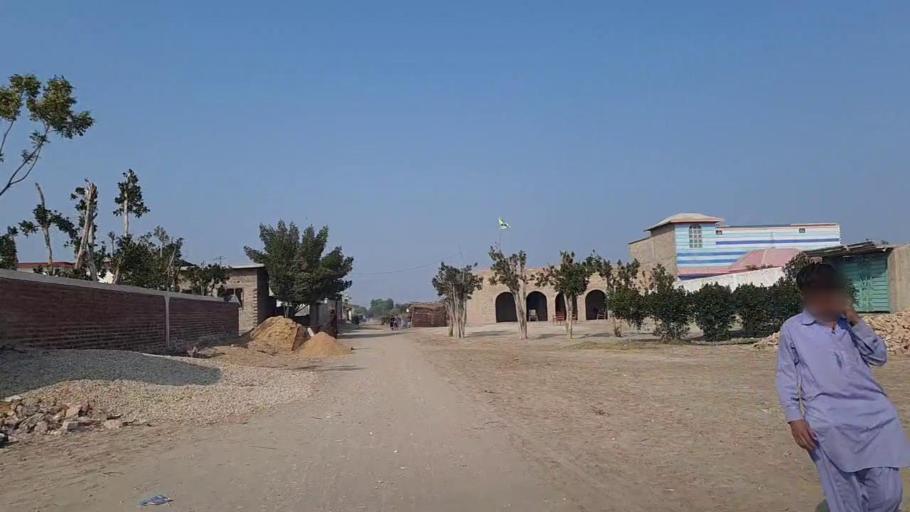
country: PK
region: Sindh
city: Daur
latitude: 26.4264
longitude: 68.4090
